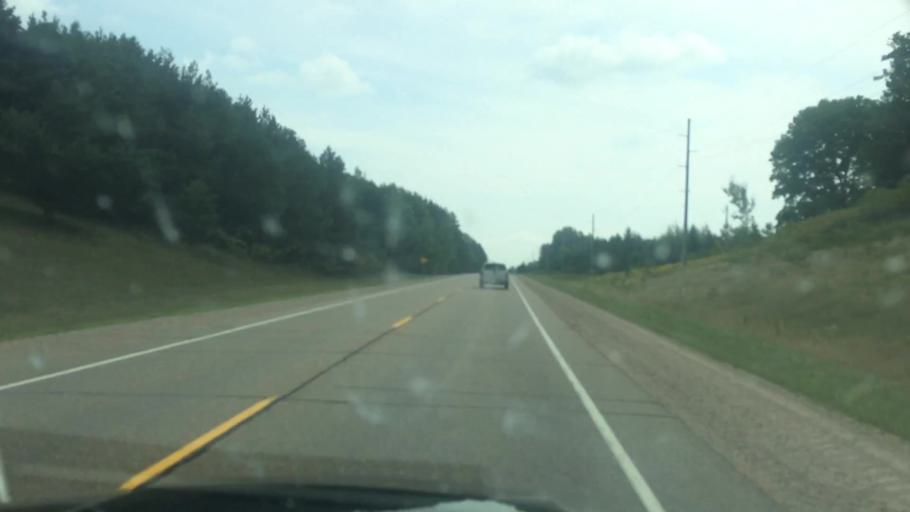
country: US
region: Wisconsin
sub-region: Langlade County
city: Antigo
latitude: 45.1618
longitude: -89.0620
